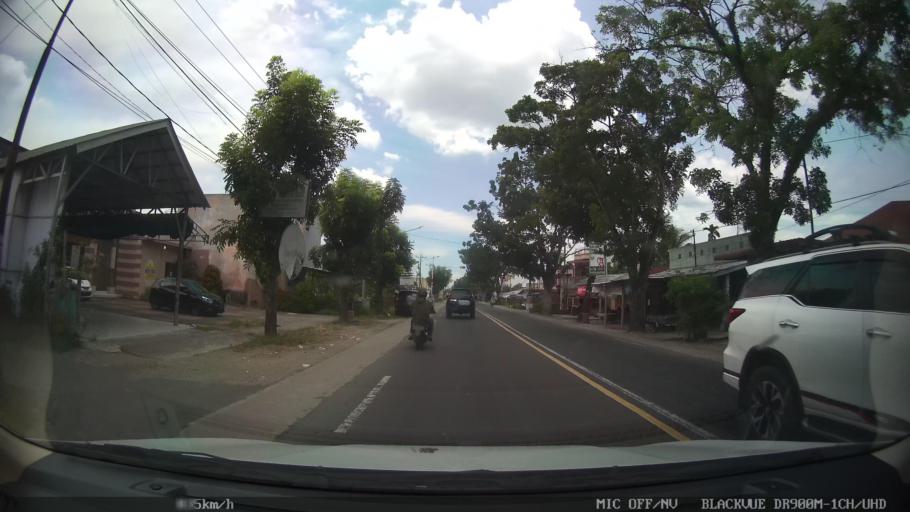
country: ID
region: North Sumatra
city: Binjai
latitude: 3.6252
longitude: 98.5062
